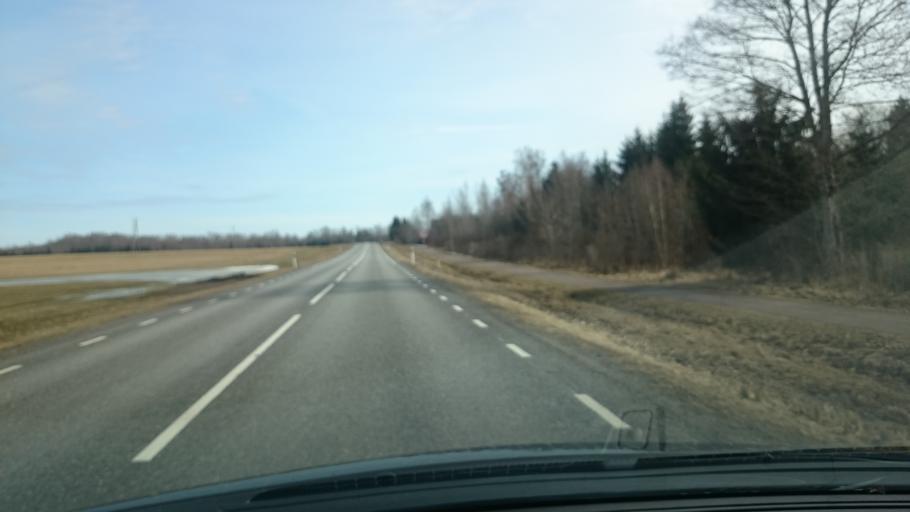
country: EE
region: Jaervamaa
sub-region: Paide linn
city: Paide
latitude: 58.8862
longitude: 25.5093
